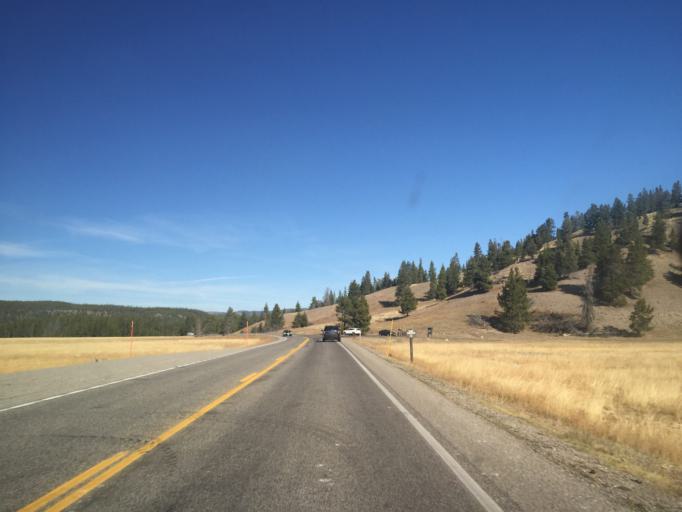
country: US
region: Montana
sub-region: Gallatin County
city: West Yellowstone
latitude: 44.5688
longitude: -110.8156
